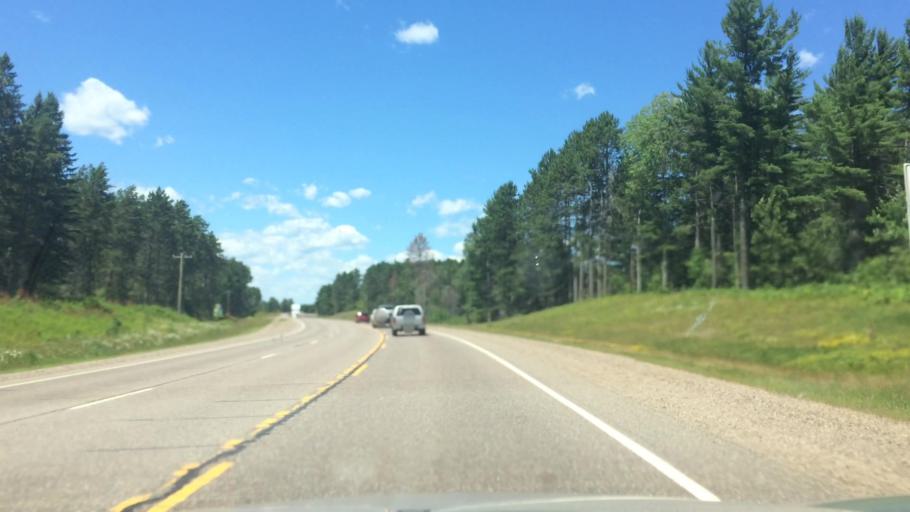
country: US
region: Wisconsin
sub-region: Lincoln County
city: Tomahawk
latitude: 45.6579
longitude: -89.7059
